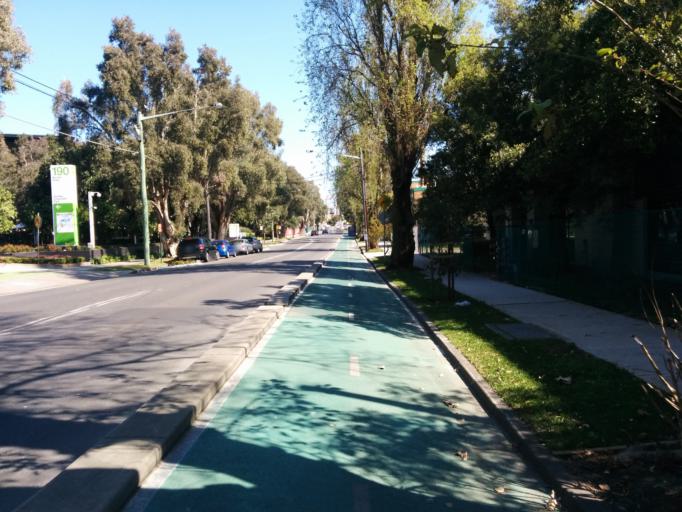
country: AU
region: New South Wales
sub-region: Botany Bay
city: Mascot
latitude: -33.9166
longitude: 151.1897
